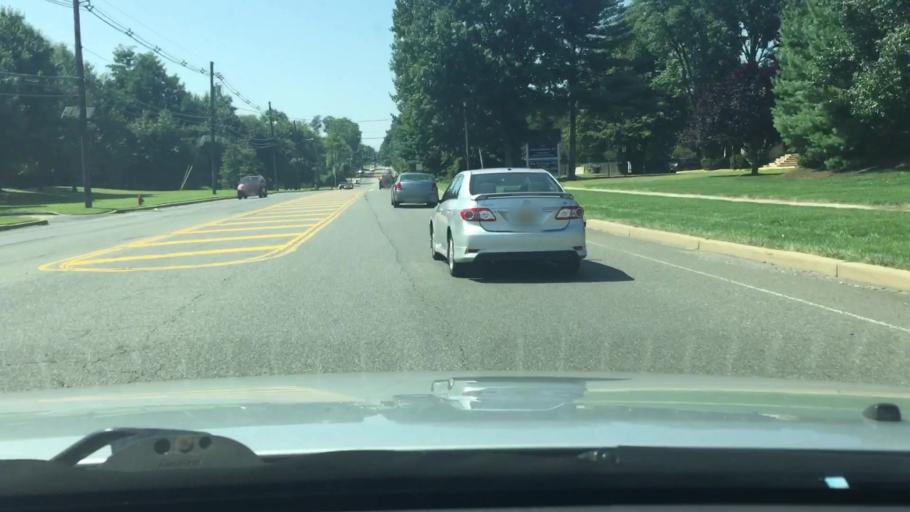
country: US
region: New Jersey
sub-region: Middlesex County
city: East Brunswick
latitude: 40.4080
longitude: -74.4216
